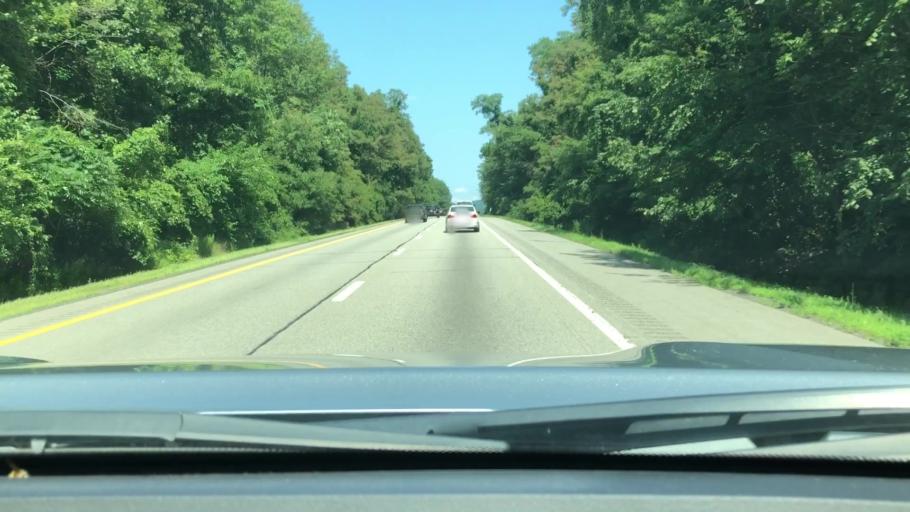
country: US
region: New York
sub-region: Dutchess County
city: Hillside Lake
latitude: 41.5358
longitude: -73.7833
